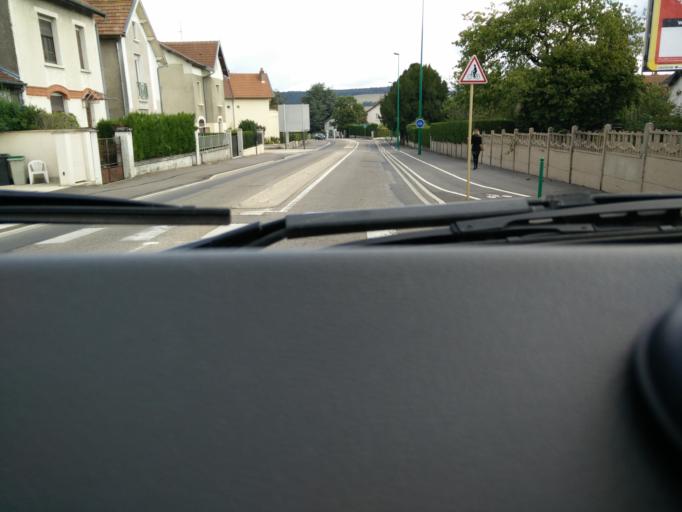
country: FR
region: Lorraine
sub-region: Departement de la Meuse
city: Verdun
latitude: 49.1525
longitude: 5.3962
